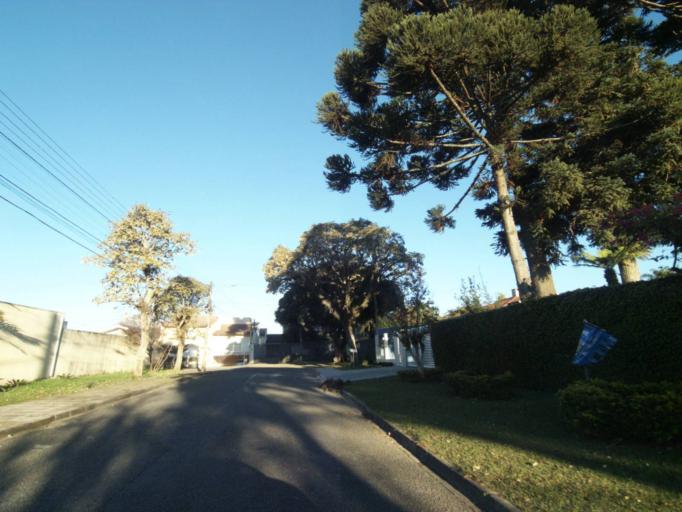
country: BR
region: Parana
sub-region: Curitiba
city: Curitiba
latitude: -25.4179
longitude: -49.2364
